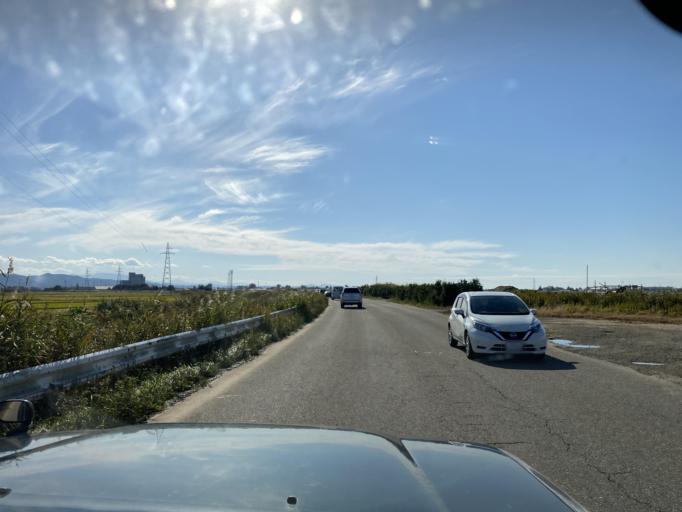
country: JP
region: Niigata
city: Niitsu-honcho
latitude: 37.8027
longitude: 139.0774
